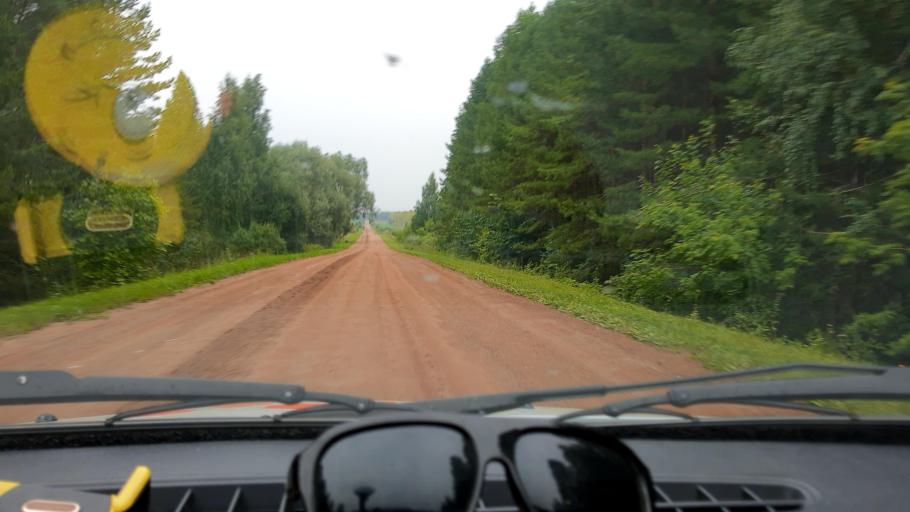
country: RU
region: Bashkortostan
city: Asanovo
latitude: 54.9791
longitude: 55.6873
